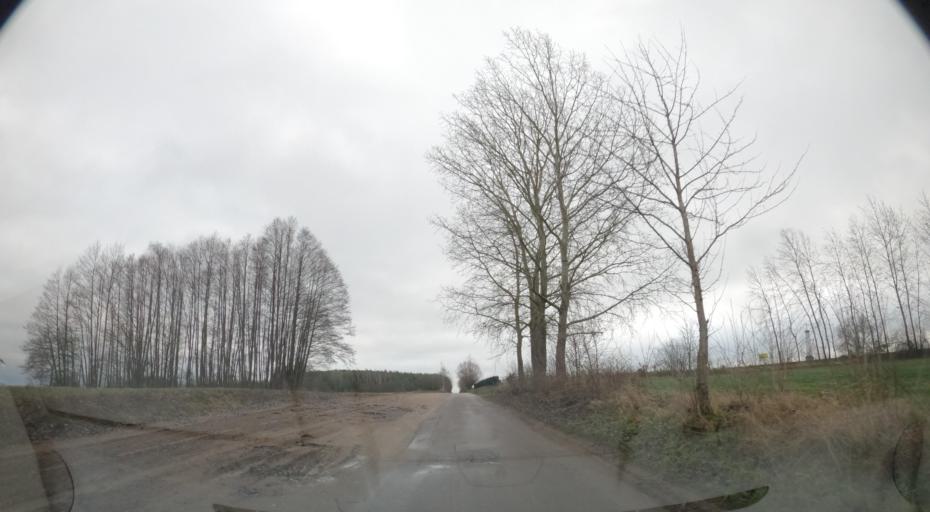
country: PL
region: Greater Poland Voivodeship
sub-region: Powiat pilski
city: Wysoka
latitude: 53.2552
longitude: 17.1296
